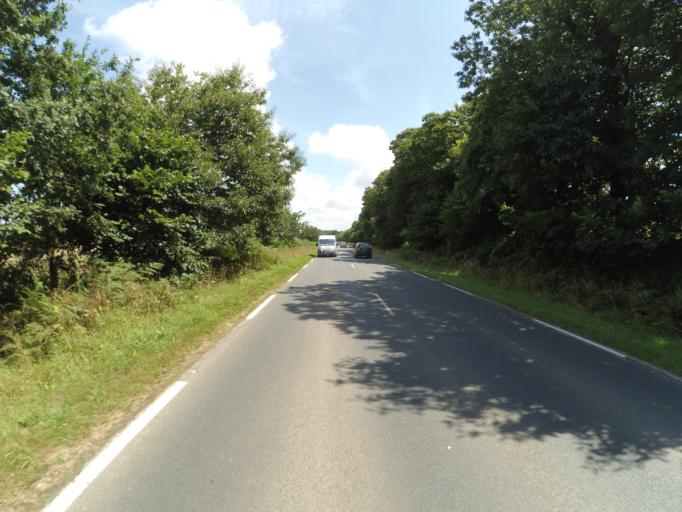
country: FR
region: Brittany
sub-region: Departement du Finistere
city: Saint-Yvi
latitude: 47.9660
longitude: -3.9193
